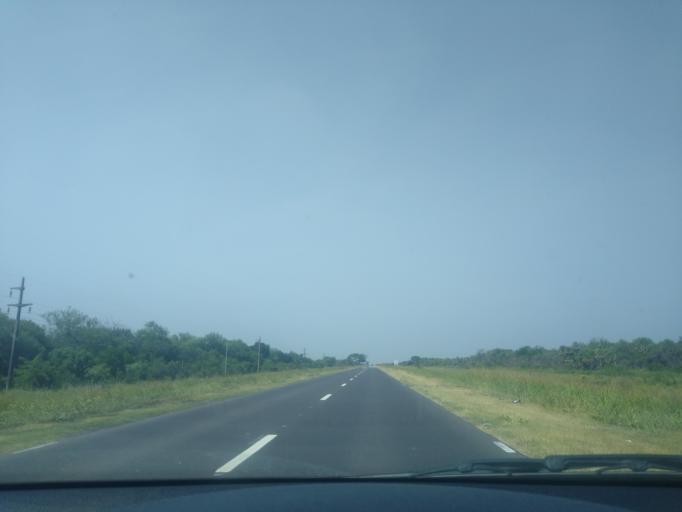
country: AR
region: Chaco
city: Fontana
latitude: -27.5485
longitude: -59.1380
